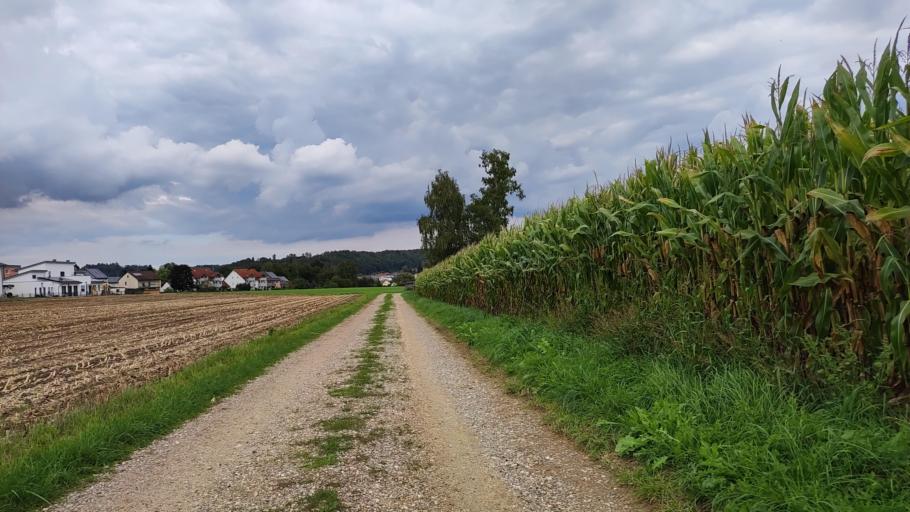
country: DE
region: Bavaria
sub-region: Swabia
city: Altenmunster
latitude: 48.4560
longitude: 10.5830
